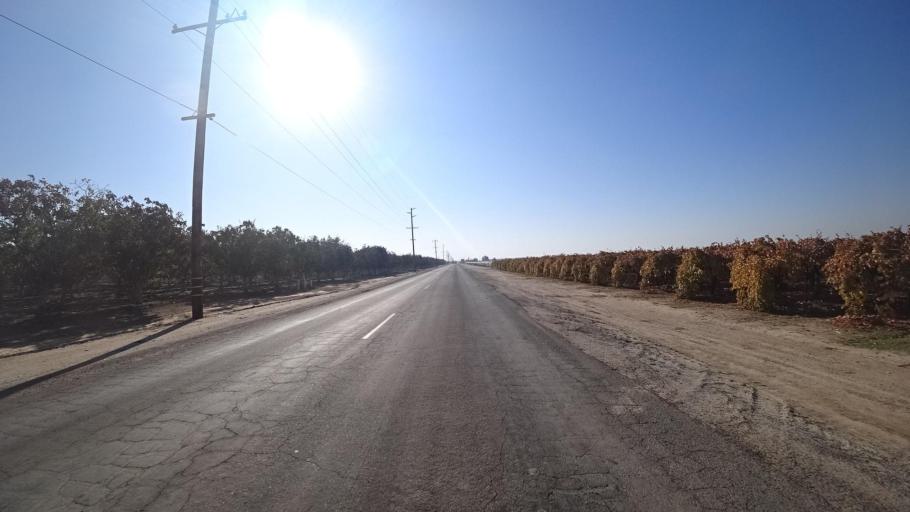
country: US
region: California
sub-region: Kern County
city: McFarland
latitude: 35.7225
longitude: -119.2051
